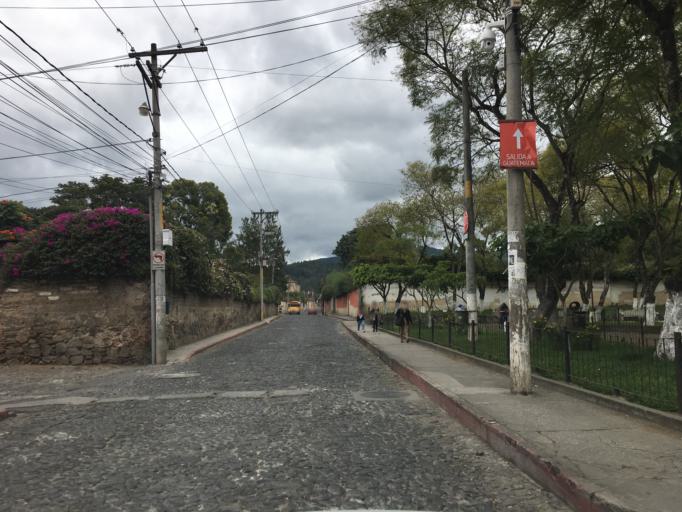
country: GT
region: Sacatepequez
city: Antigua Guatemala
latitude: 14.5515
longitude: -90.7286
